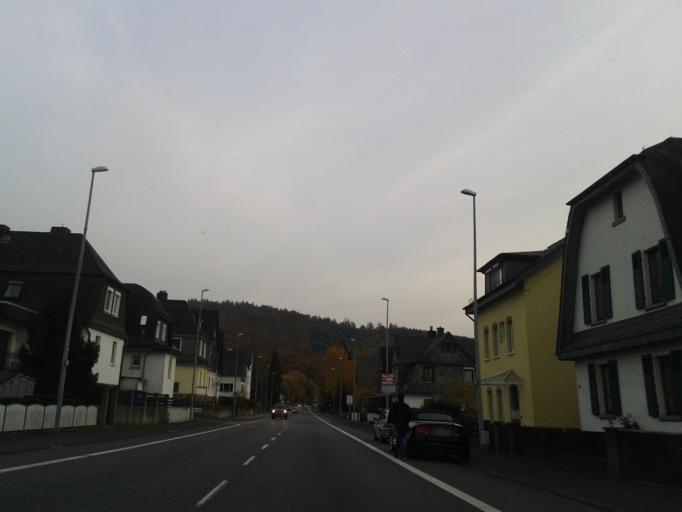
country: DE
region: Hesse
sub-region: Regierungsbezirk Giessen
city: Sinn
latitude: 50.6492
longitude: 8.3300
